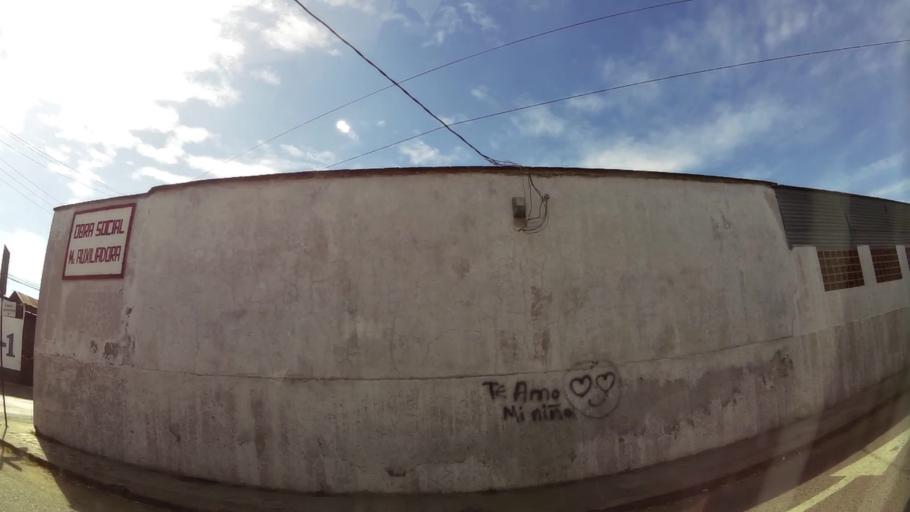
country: SV
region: Santa Ana
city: Chalchuapa
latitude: 13.9816
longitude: -89.6803
